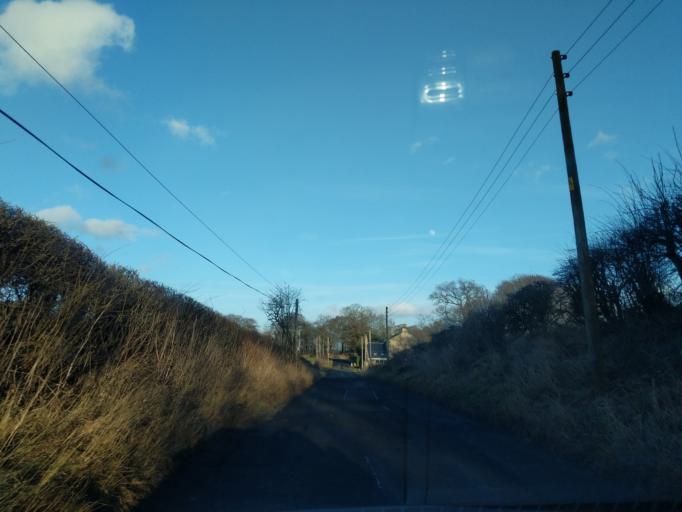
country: GB
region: Scotland
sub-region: Edinburgh
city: Balerno
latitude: 55.9035
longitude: -3.3294
